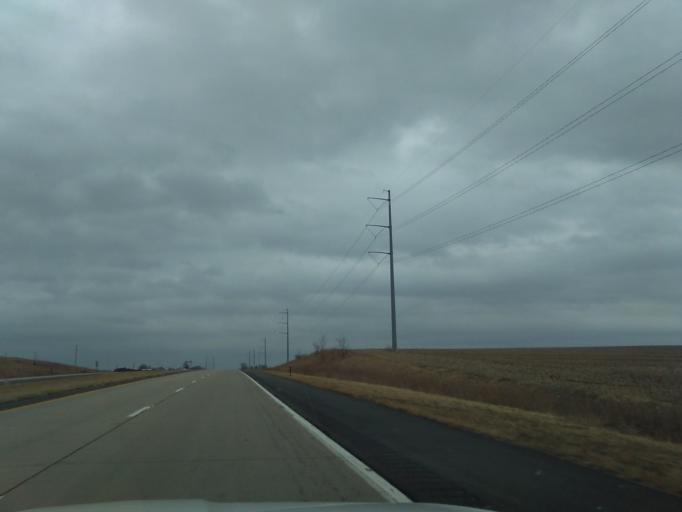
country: US
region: Nebraska
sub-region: Otoe County
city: Syracuse
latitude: 40.6682
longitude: -96.1407
